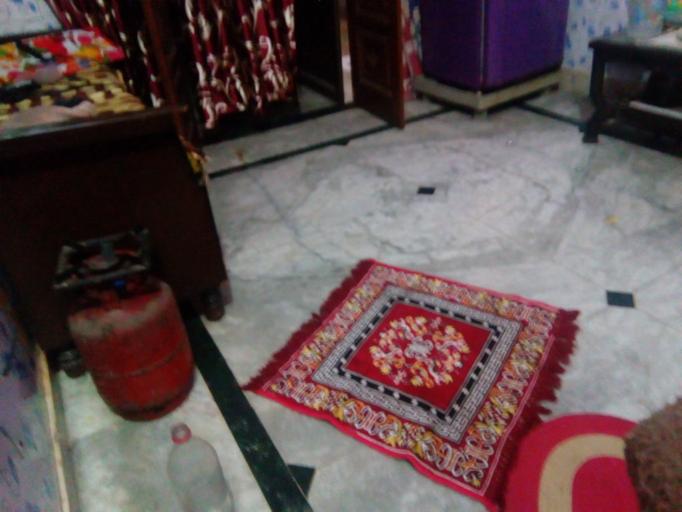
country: IN
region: NCT
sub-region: North Delhi
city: Delhi
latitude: 28.6711
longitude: 77.2594
